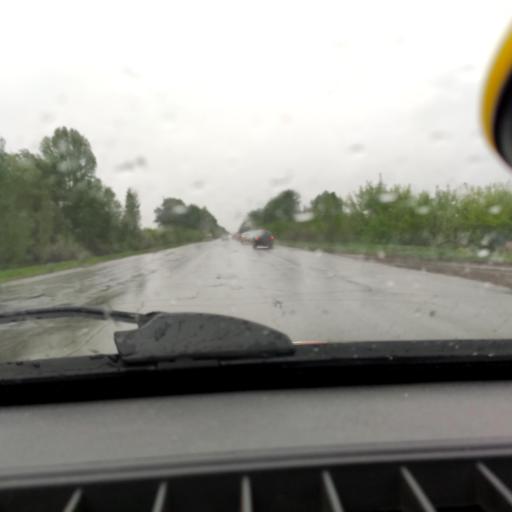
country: RU
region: Samara
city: Tol'yatti
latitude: 53.6340
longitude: 49.4183
